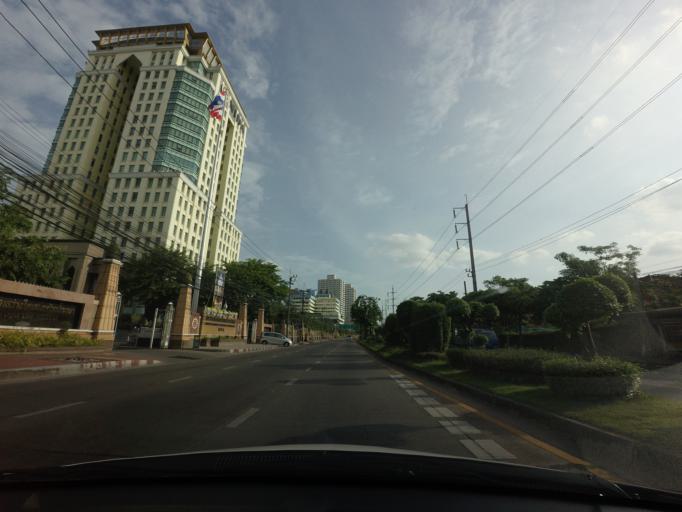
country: TH
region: Bangkok
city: Bang Kapi
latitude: 13.7717
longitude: 100.6539
